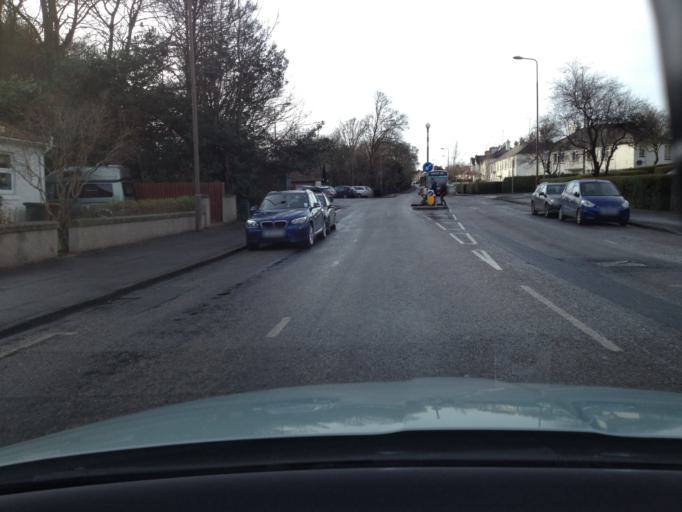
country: GB
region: Scotland
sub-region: Edinburgh
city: Edinburgh
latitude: 55.9261
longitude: -3.1921
